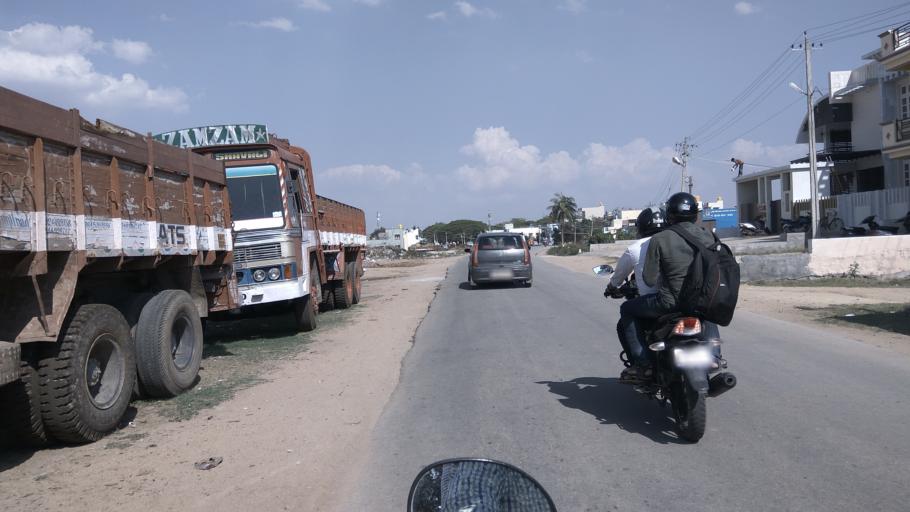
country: IN
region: Karnataka
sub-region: Kolar
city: Mulbagal
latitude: 13.1623
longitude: 78.3805
